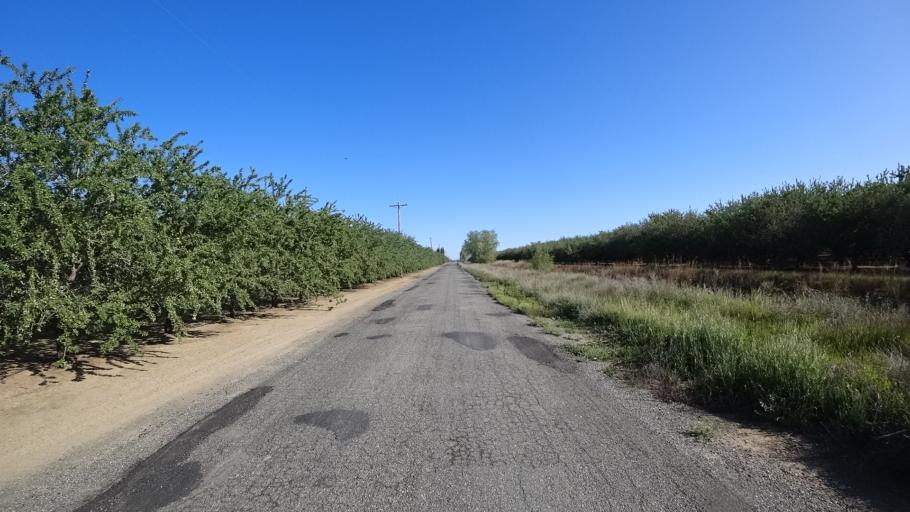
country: US
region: California
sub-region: Glenn County
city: Hamilton City
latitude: 39.6960
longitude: -122.0547
